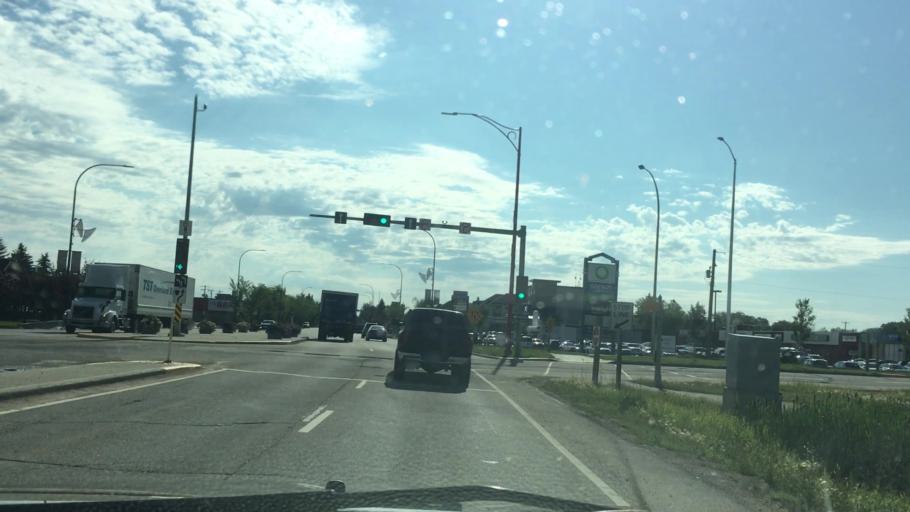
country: CA
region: Alberta
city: Leduc
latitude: 53.2647
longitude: -113.5623
